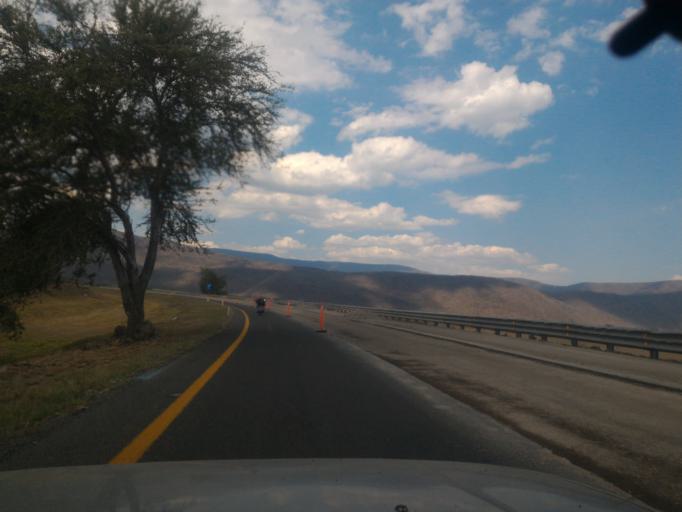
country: MX
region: Jalisco
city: Zacoalco de Torres
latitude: 20.1593
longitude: -103.5010
